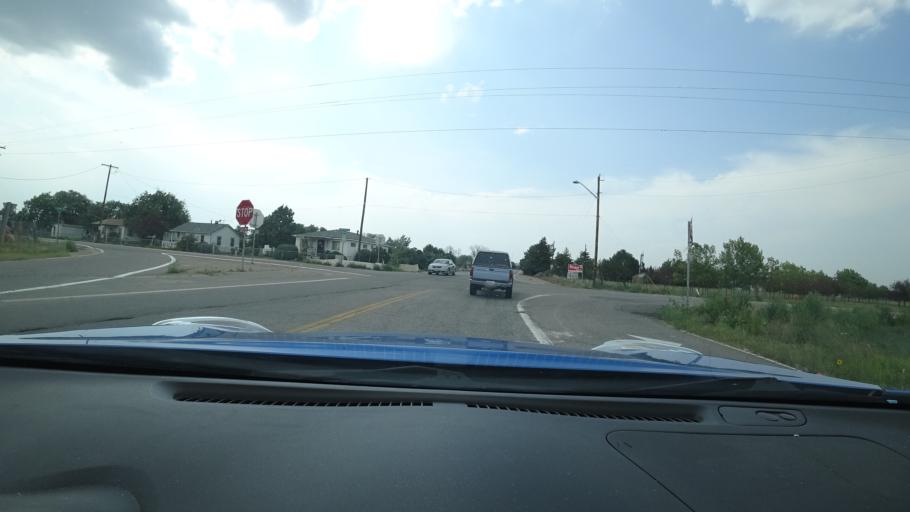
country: US
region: Colorado
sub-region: Adams County
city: Todd Creek
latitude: 39.9216
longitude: -104.8647
